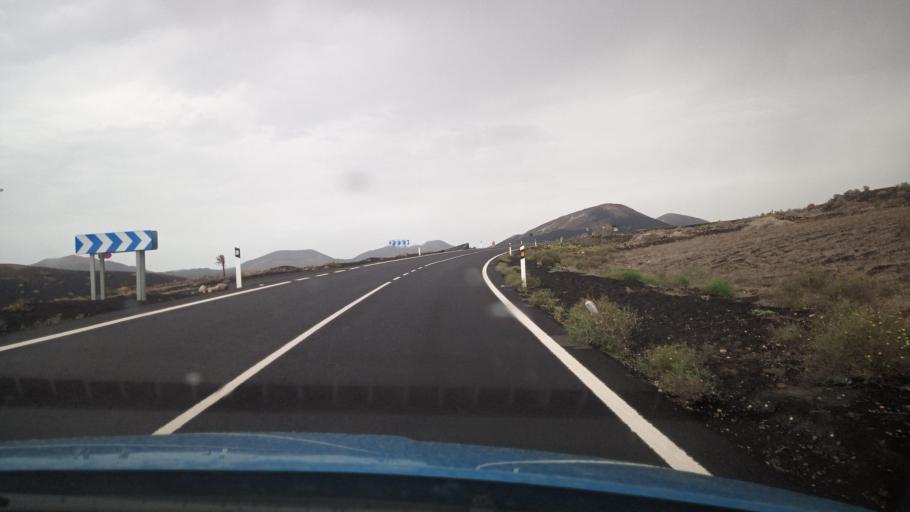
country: ES
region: Canary Islands
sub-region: Provincia de Las Palmas
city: Yaiza
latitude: 28.9514
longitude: -13.7388
